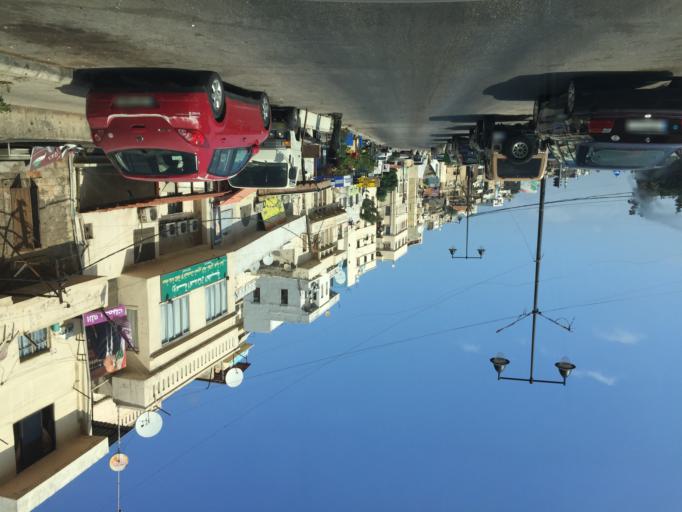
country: LB
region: Liban-Nord
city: Tripoli
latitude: 34.4337
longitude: 35.8462
